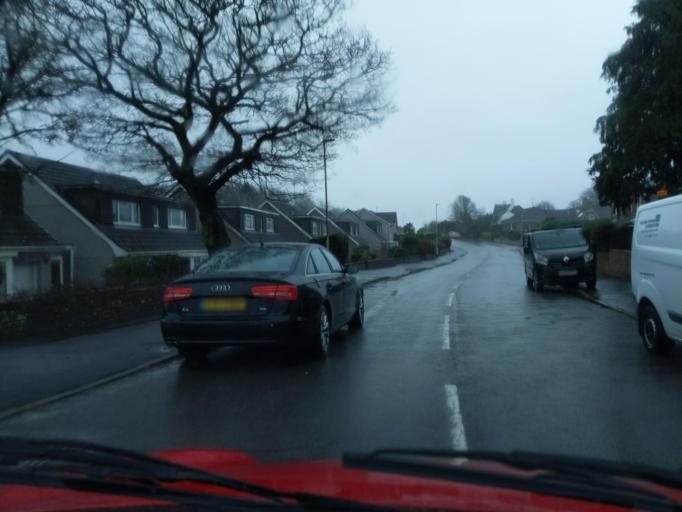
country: GB
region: England
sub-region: Plymouth
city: Plymstock
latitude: 50.4010
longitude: -4.1063
